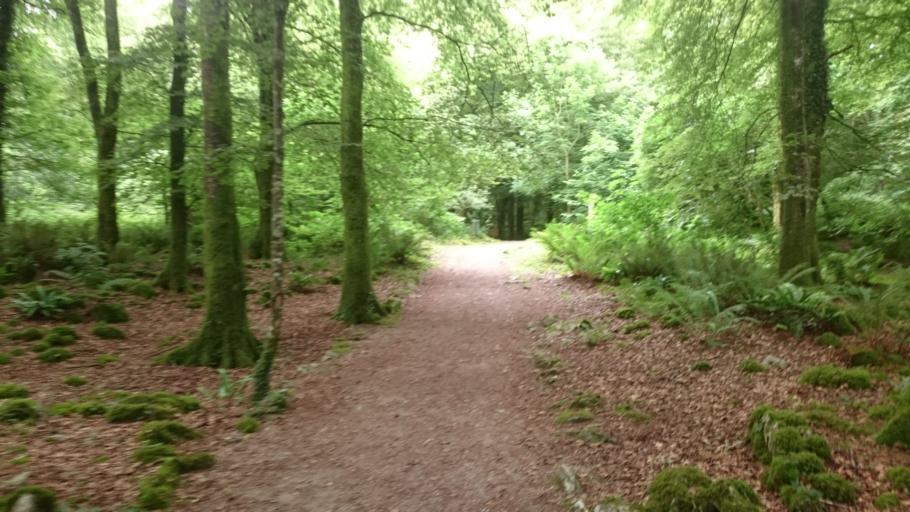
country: IE
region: Munster
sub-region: An Clar
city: Sixmilebridge
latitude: 52.8105
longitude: -8.7966
